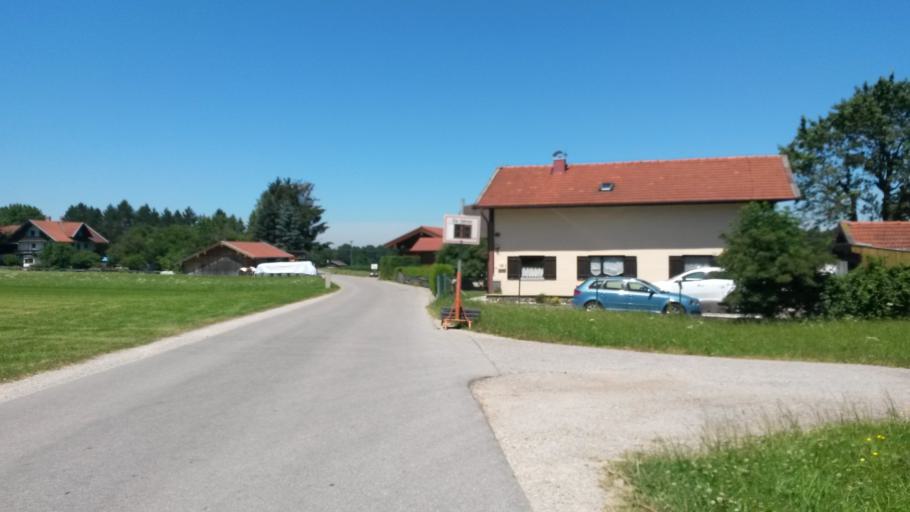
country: DE
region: Bavaria
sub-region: Upper Bavaria
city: Bernau am Chiemsee
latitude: 47.7964
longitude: 12.4123
